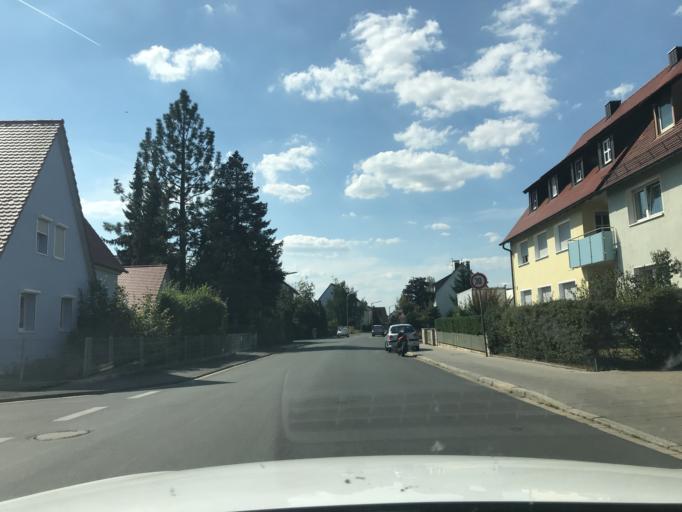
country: DE
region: Bavaria
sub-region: Regierungsbezirk Mittelfranken
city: Erlangen
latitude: 49.5662
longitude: 11.0003
